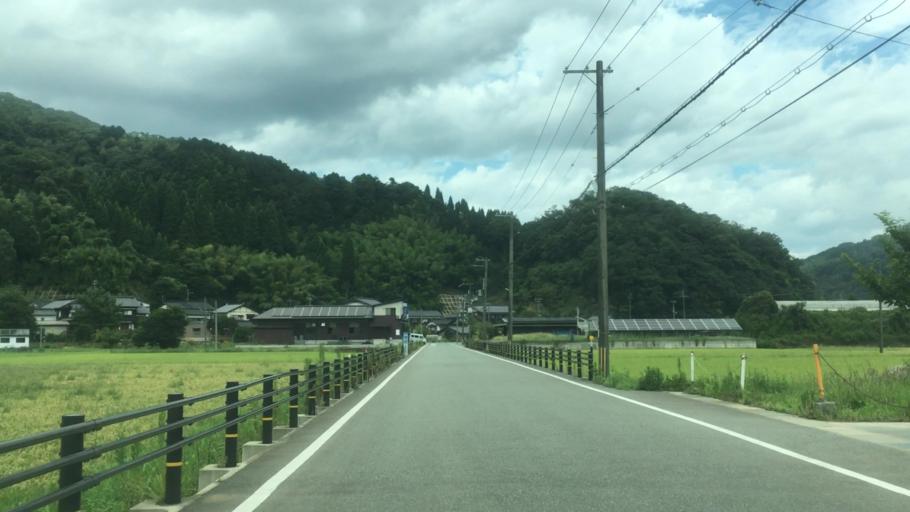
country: JP
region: Hyogo
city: Toyooka
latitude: 35.5918
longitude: 134.7984
